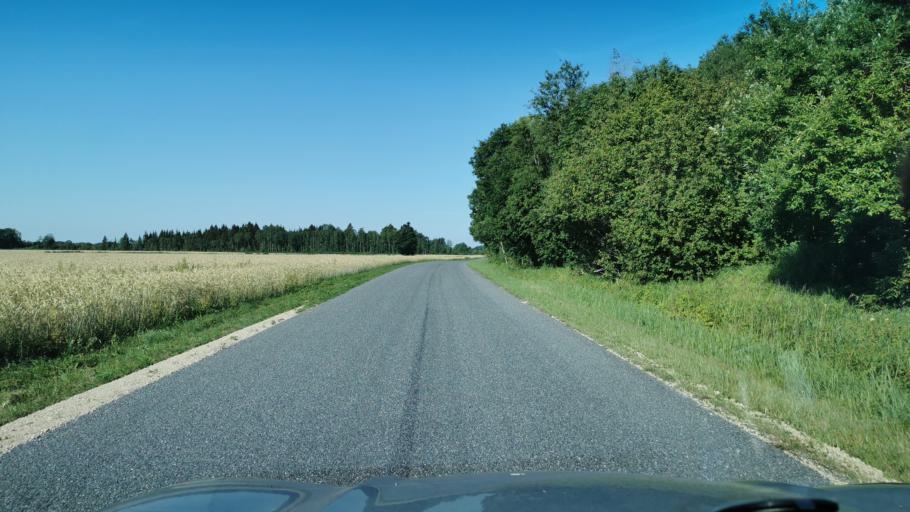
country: EE
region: Harju
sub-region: Paldiski linn
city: Paldiski
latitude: 59.2128
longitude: 24.0306
